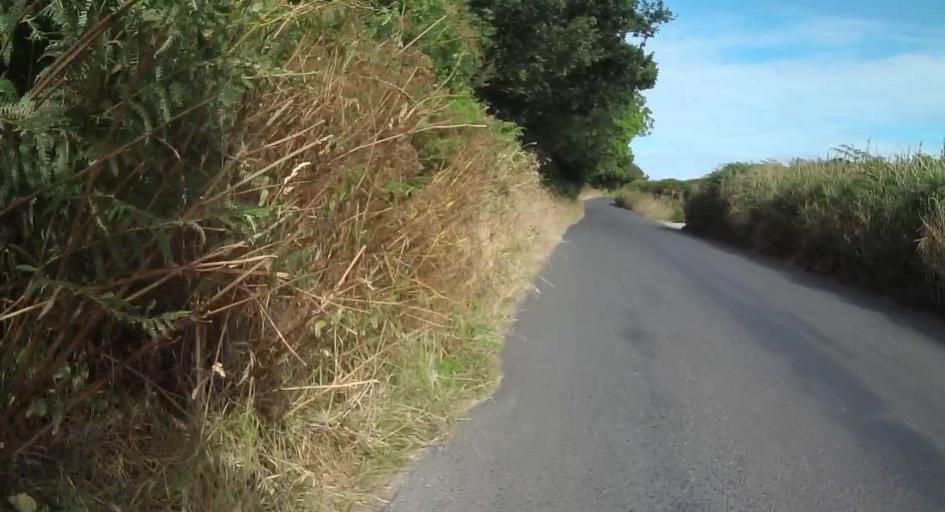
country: GB
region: England
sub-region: Dorset
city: Wareham
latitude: 50.6761
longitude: -2.1037
